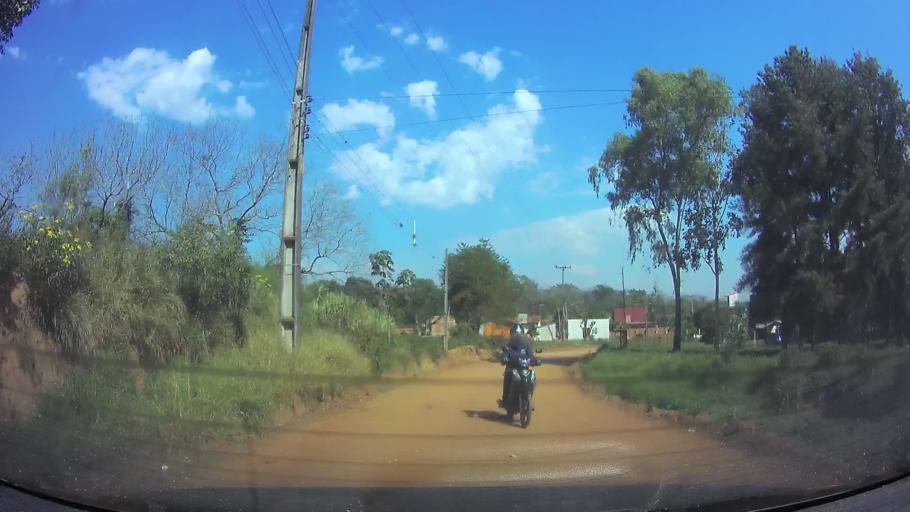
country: PY
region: Central
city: Limpio
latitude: -25.2285
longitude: -57.4402
